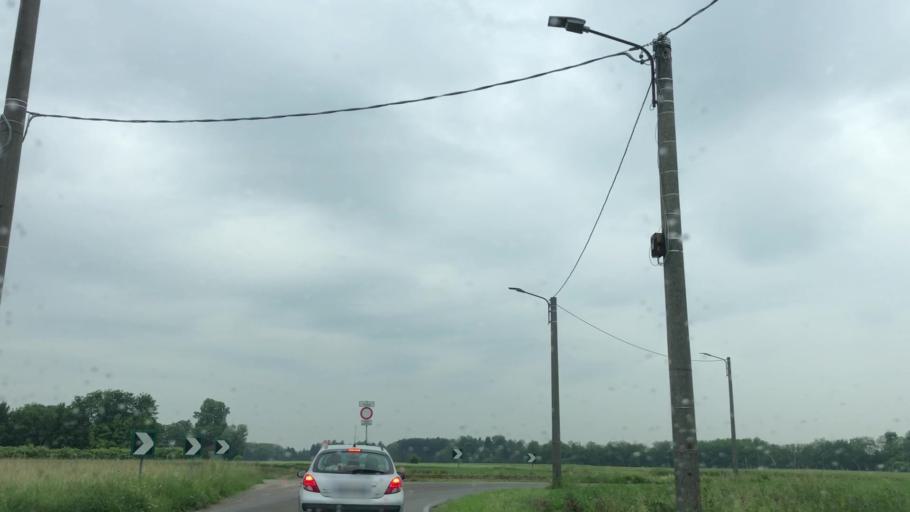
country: IT
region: Lombardy
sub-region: Provincia di Como
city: Fenegro
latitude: 45.6929
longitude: 8.9936
